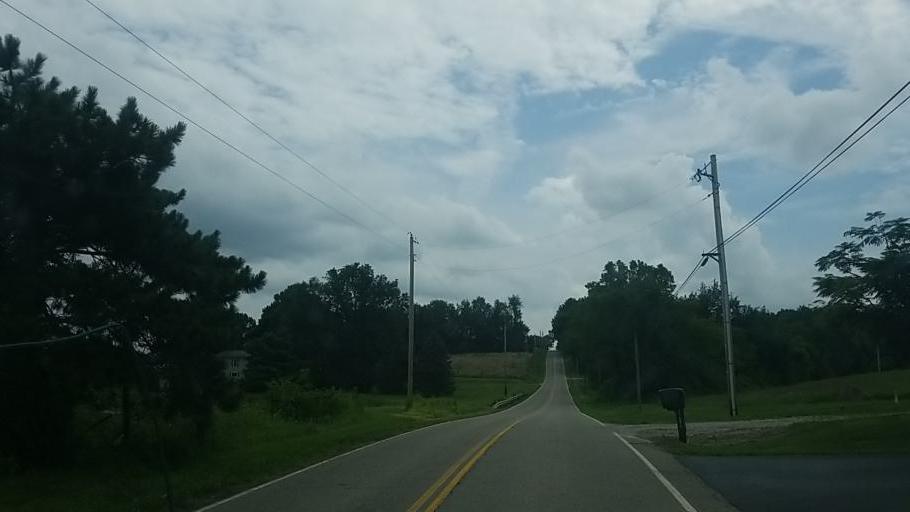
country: US
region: Ohio
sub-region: Licking County
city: Utica
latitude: 40.2239
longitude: -82.3658
